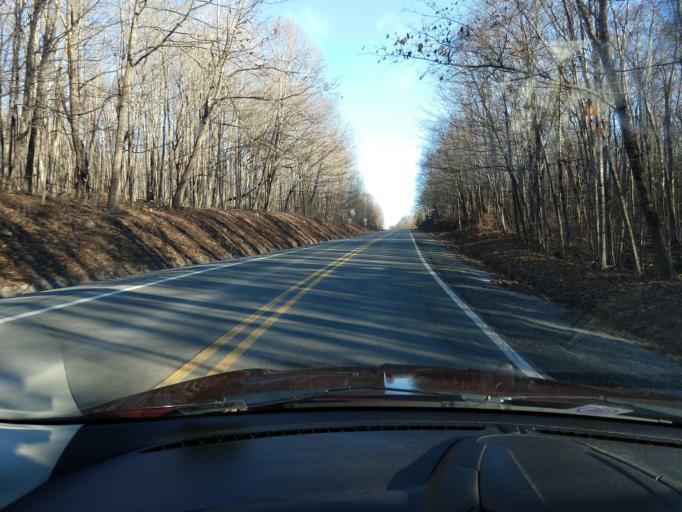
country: US
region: Virginia
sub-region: Highland County
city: Monterey
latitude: 38.5665
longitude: -79.8426
